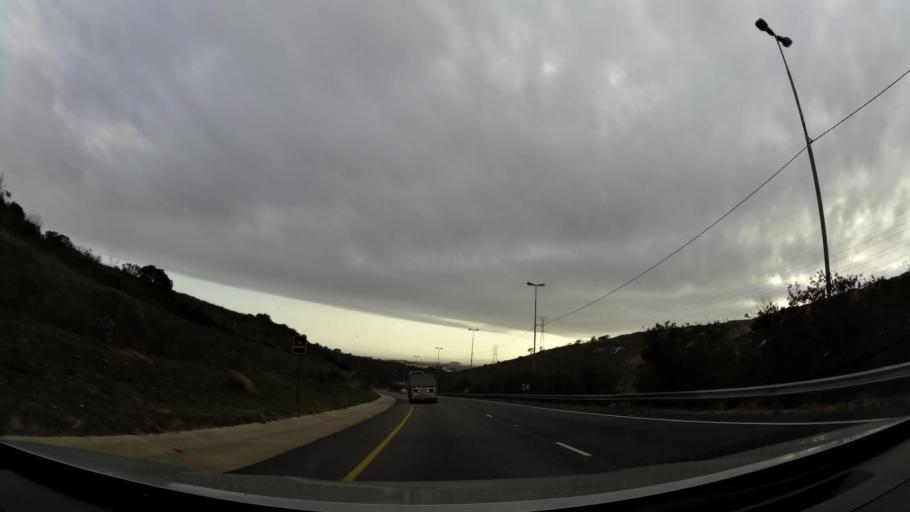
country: ZA
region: Eastern Cape
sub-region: Nelson Mandela Bay Metropolitan Municipality
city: Port Elizabeth
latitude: -33.9335
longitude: 25.5573
